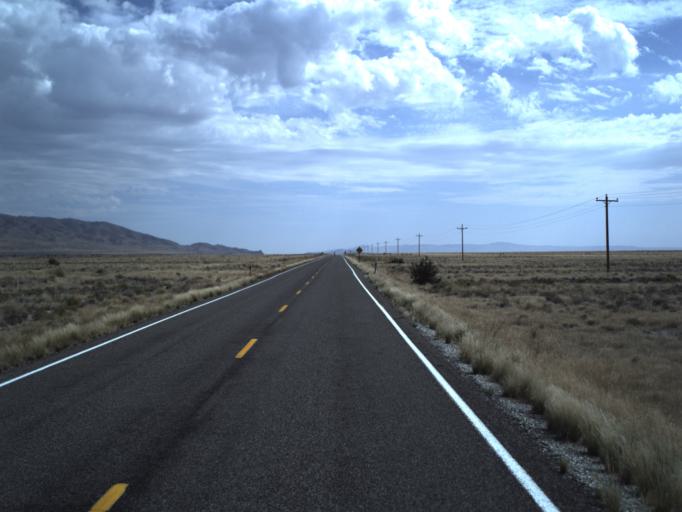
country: US
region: Utah
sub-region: Tooele County
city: Wendover
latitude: 41.4294
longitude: -113.8144
